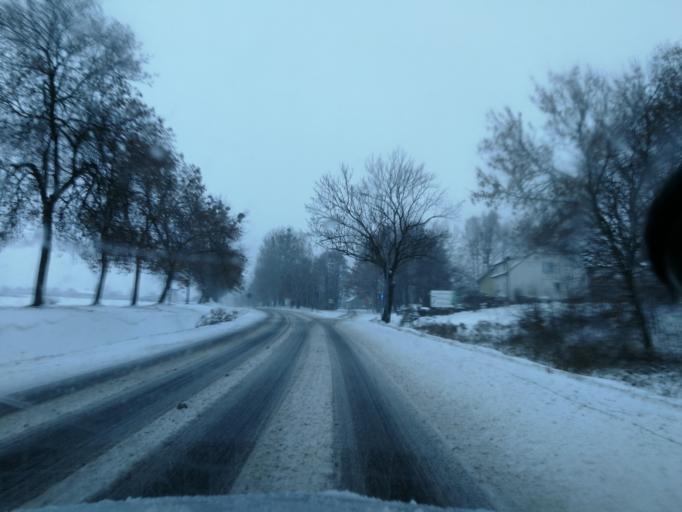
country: PL
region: Silesian Voivodeship
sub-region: Powiat pszczynski
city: Pszczyna
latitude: 49.9865
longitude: 18.9240
